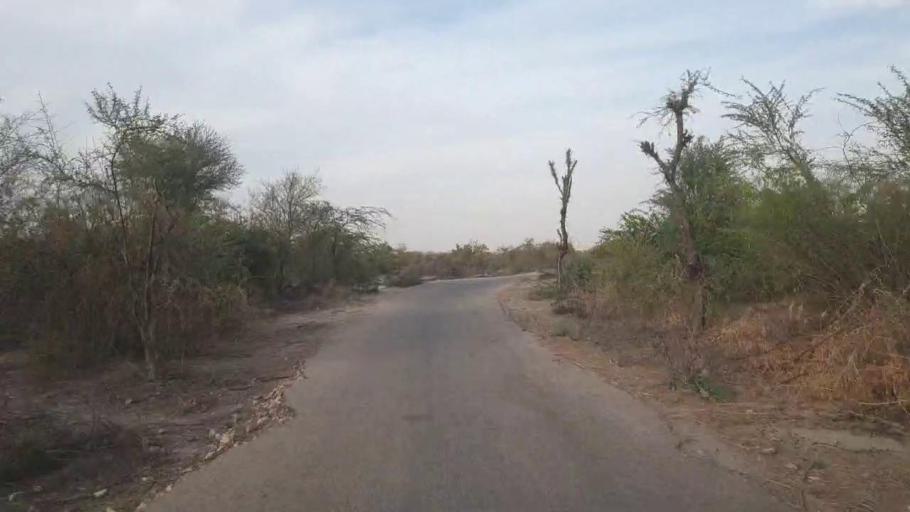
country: PK
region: Sindh
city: Nabisar
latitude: 25.1111
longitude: 69.6780
